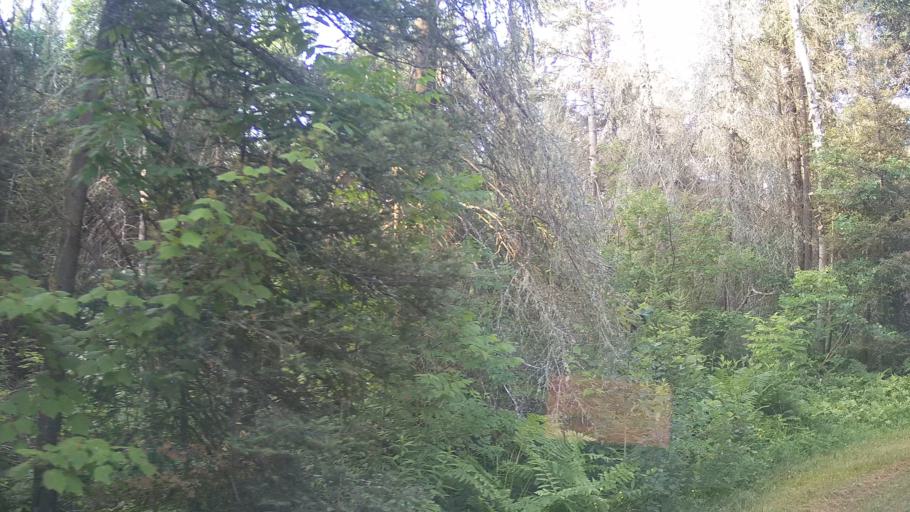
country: CA
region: Ontario
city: Rayside-Balfour
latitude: 46.5741
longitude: -81.3125
